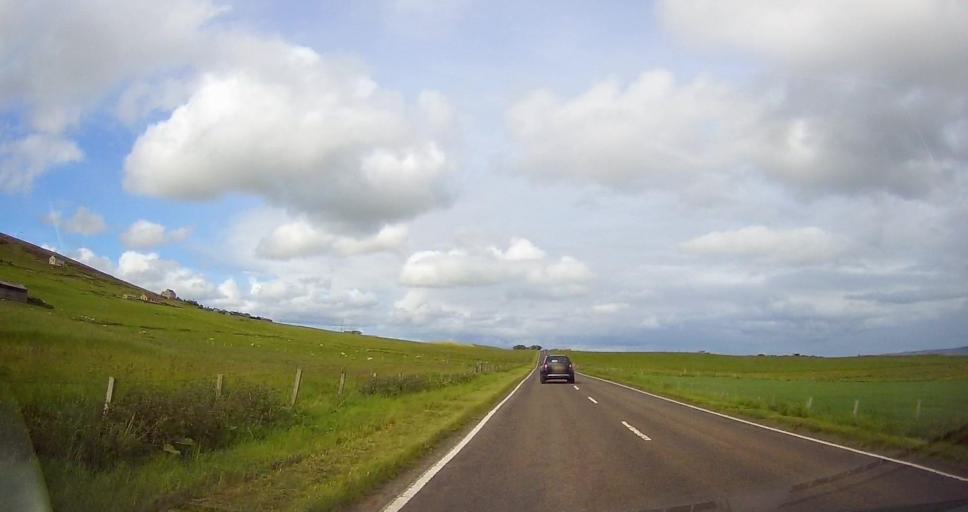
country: GB
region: Scotland
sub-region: Orkney Islands
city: Orkney
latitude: 59.0157
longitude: -3.1060
